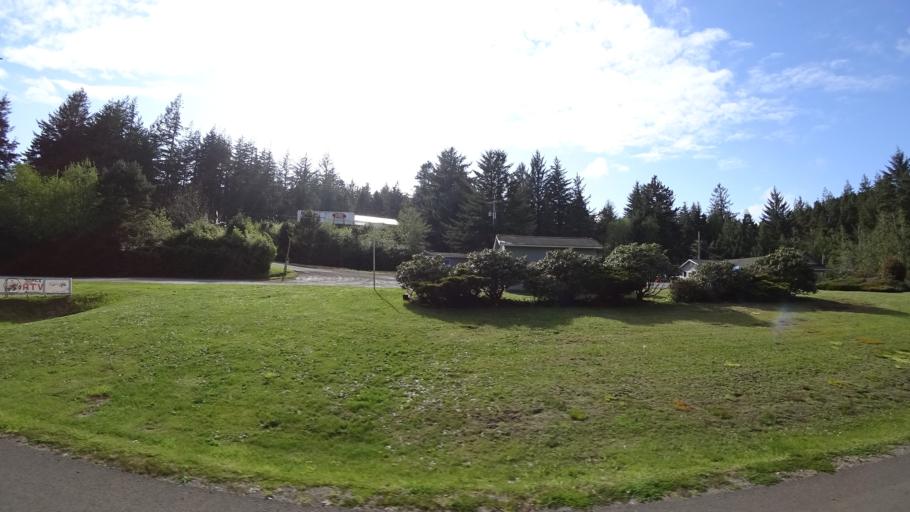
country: US
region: Oregon
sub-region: Lane County
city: Dunes City
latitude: 43.9138
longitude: -124.1110
